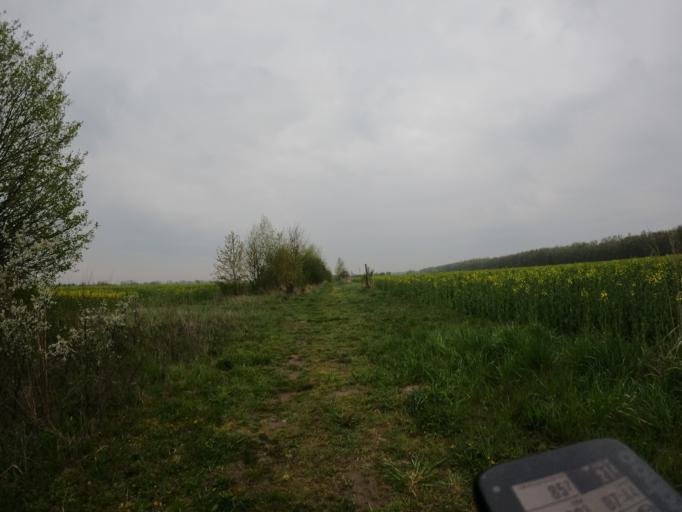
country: DE
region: Berlin
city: Lichtenrade
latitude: 52.3941
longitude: 13.4289
